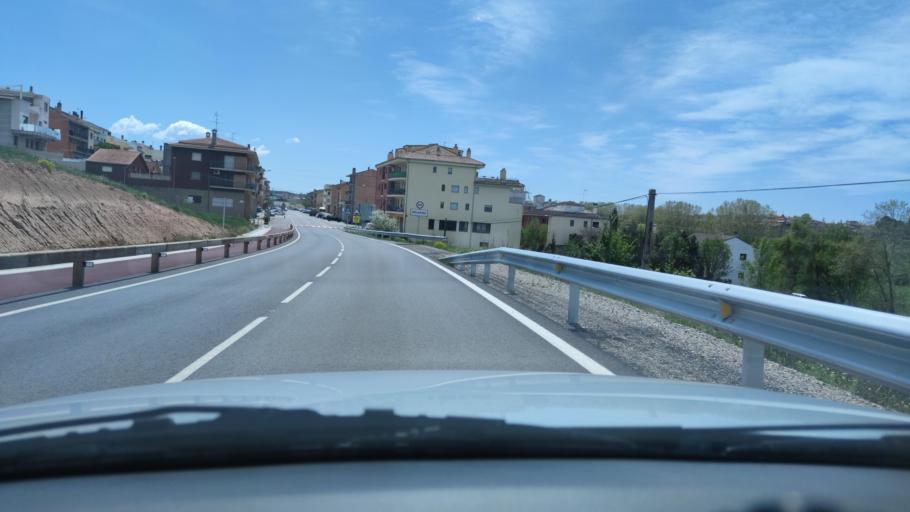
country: ES
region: Catalonia
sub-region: Provincia de Lleida
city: Solsona
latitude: 42.0018
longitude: 1.5174
